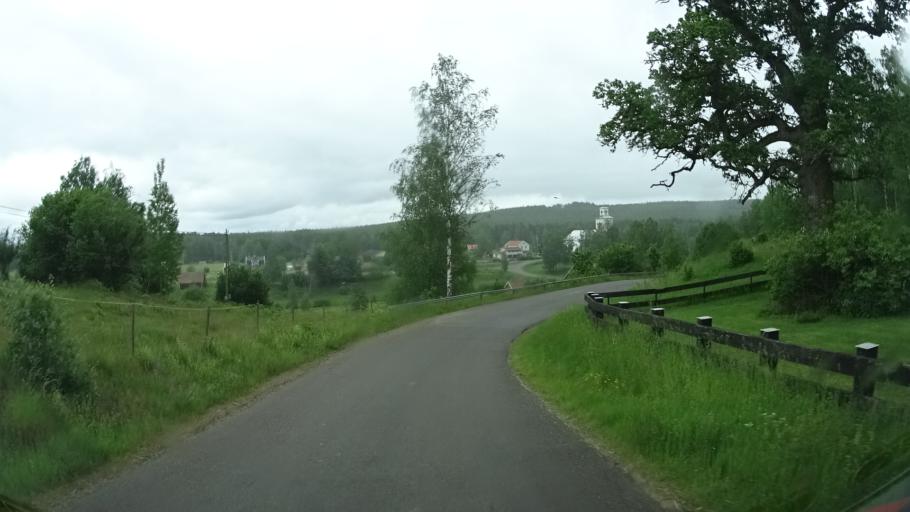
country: SE
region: Joenkoeping
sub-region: Eksjo Kommun
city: Mariannelund
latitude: 57.6770
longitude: 15.5856
